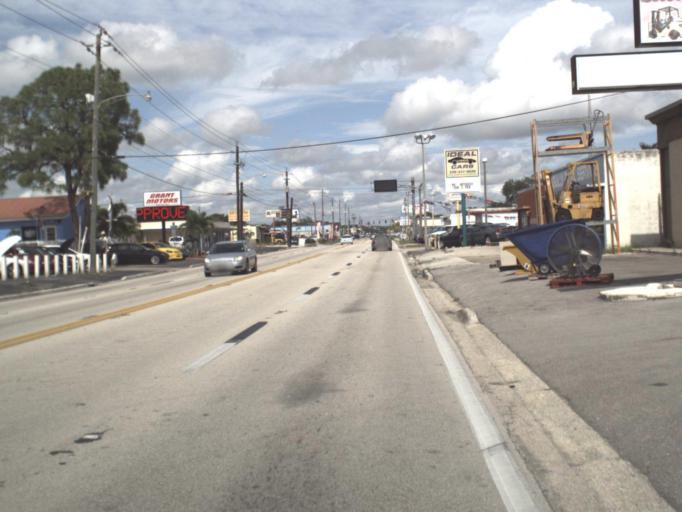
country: US
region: Florida
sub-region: Lee County
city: Fort Myers
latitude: 26.6265
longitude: -81.8620
